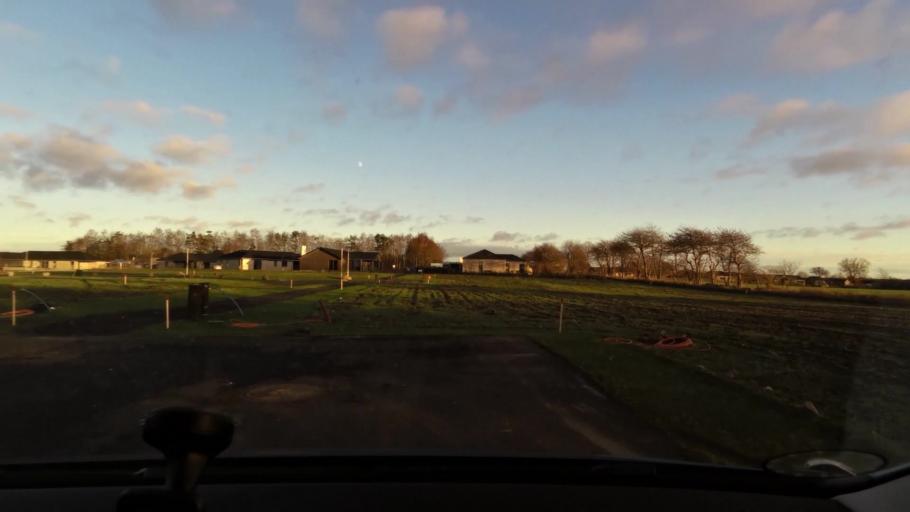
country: DK
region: Zealand
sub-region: Soro Kommune
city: Frederiksberg
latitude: 55.4092
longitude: 11.5510
